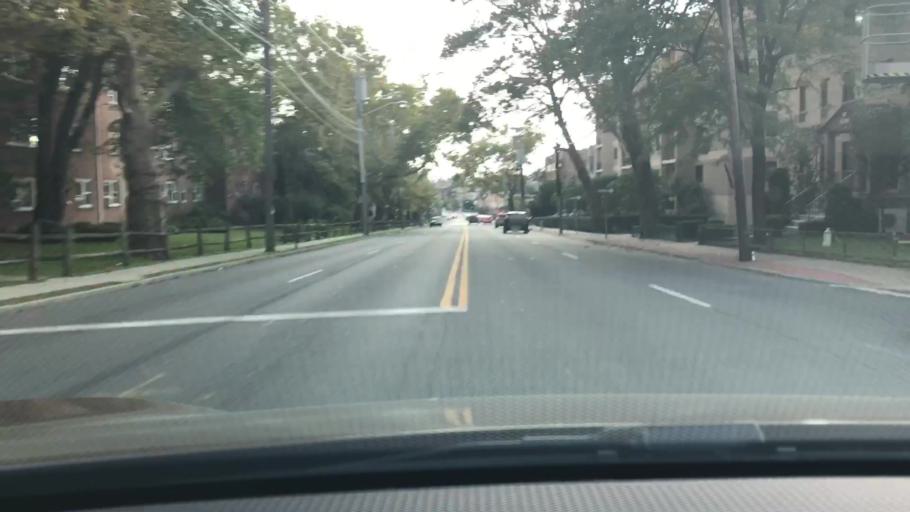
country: US
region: New York
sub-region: Westchester County
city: Tuckahoe
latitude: 40.9599
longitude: -73.8121
